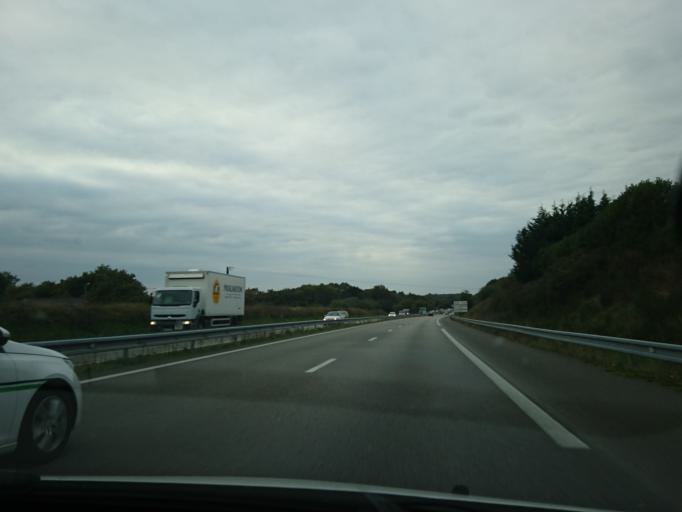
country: FR
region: Brittany
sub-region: Departement du Morbihan
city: Surzur
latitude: 47.6037
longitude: -2.5977
